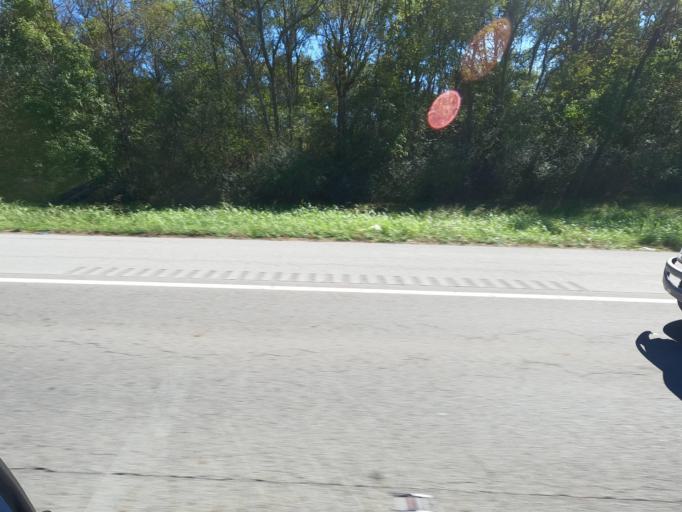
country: US
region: Tennessee
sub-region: Maury County
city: Mount Pleasant
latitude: 35.5704
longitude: -87.1618
